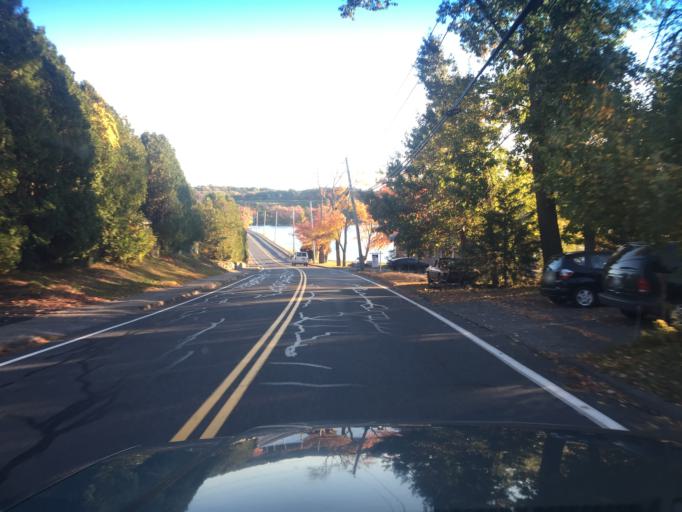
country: US
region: Massachusetts
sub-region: Middlesex County
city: Hudson
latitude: 42.3712
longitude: -71.5546
